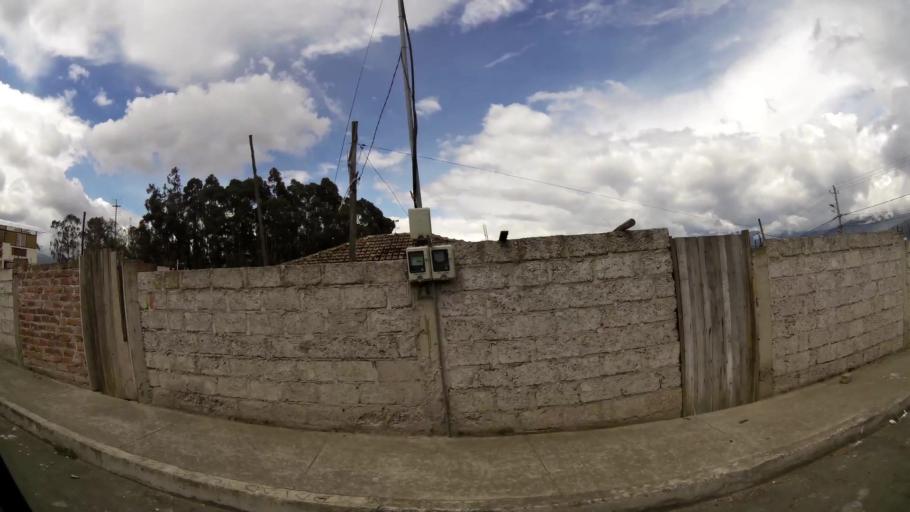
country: EC
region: Tungurahua
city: Ambato
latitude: -1.2635
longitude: -78.6086
